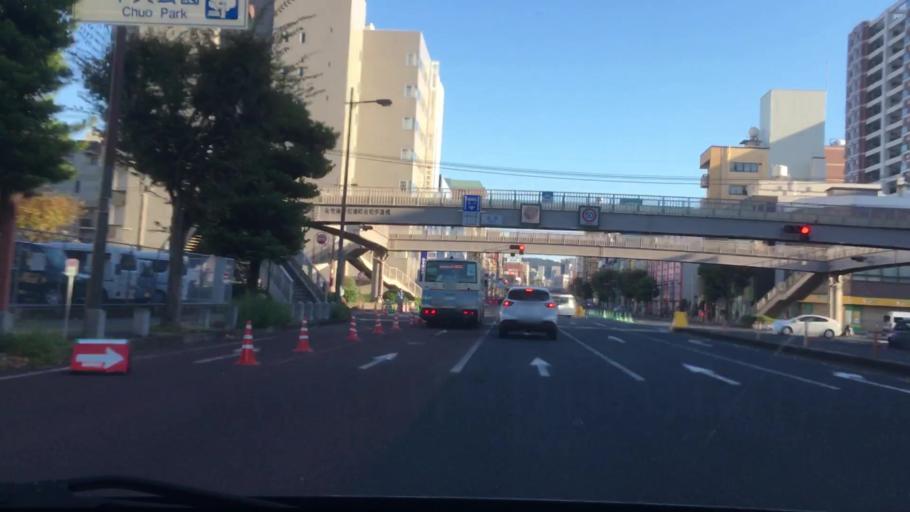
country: JP
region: Nagasaki
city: Sasebo
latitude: 33.1754
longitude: 129.7188
